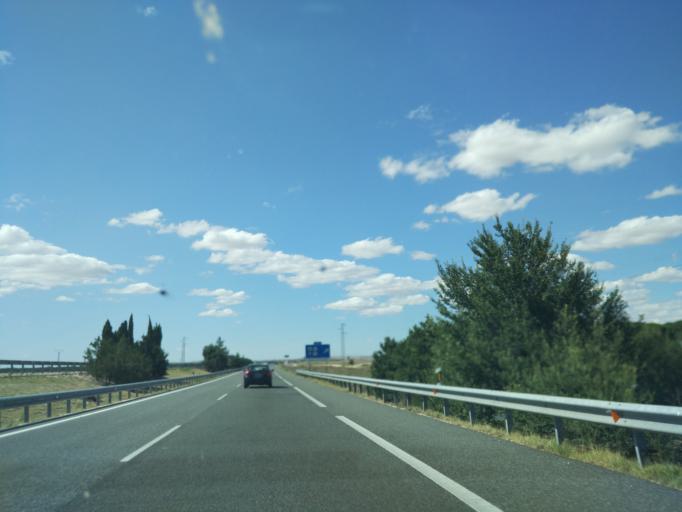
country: ES
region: Castille and Leon
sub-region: Provincia de Valladolid
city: San Vicente del Palacio
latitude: 41.2618
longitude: -4.8787
